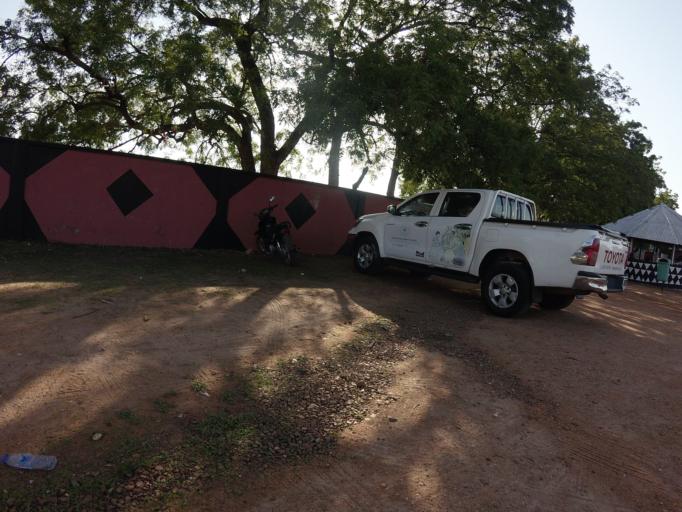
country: GH
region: Upper East
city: Navrongo
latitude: 10.9844
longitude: -1.1078
